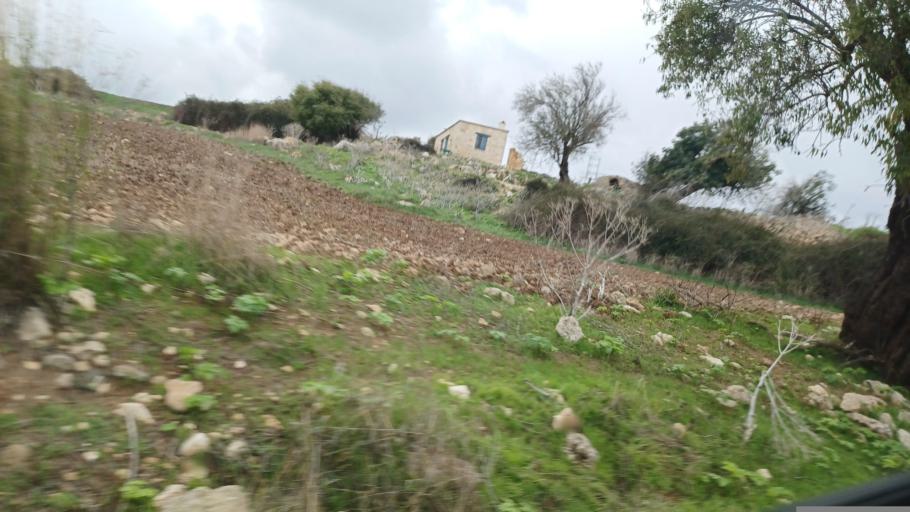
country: CY
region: Pafos
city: Polis
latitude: 34.9827
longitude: 32.3711
